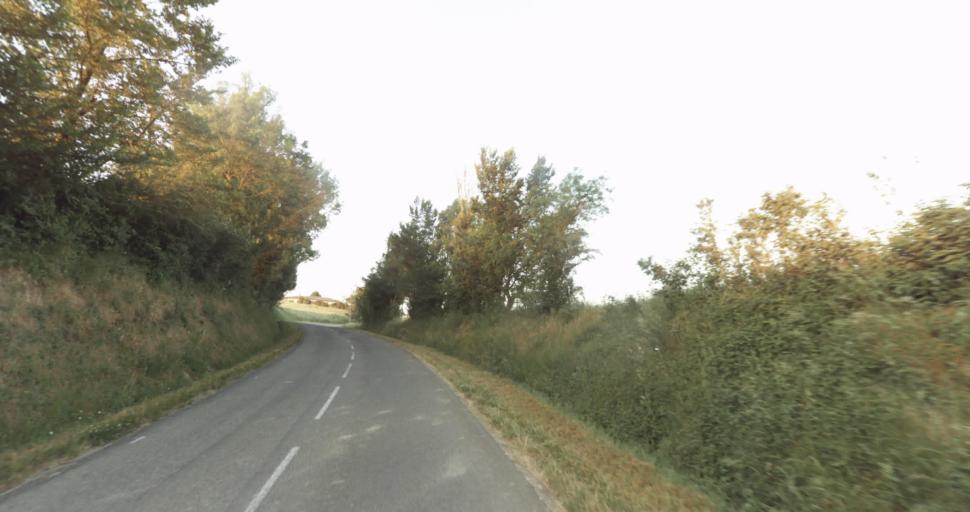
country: FR
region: Midi-Pyrenees
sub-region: Departement du Gers
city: Pujaudran
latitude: 43.6555
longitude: 1.1088
